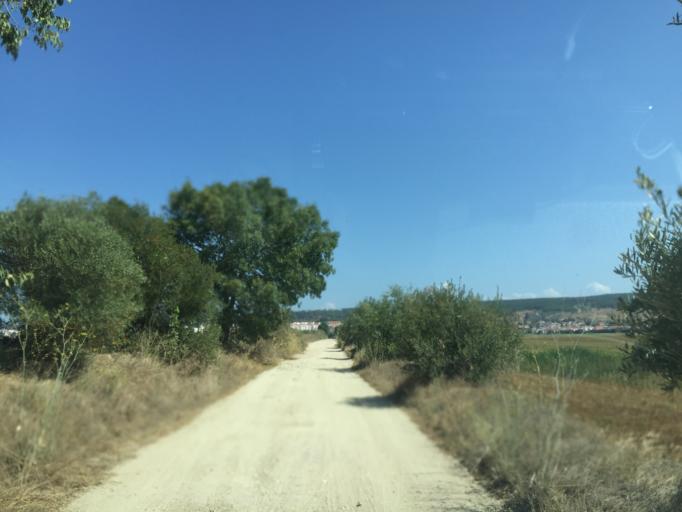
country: PT
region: Santarem
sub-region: Chamusca
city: Vila Nova da Barquinha
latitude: 39.4537
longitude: -8.4458
